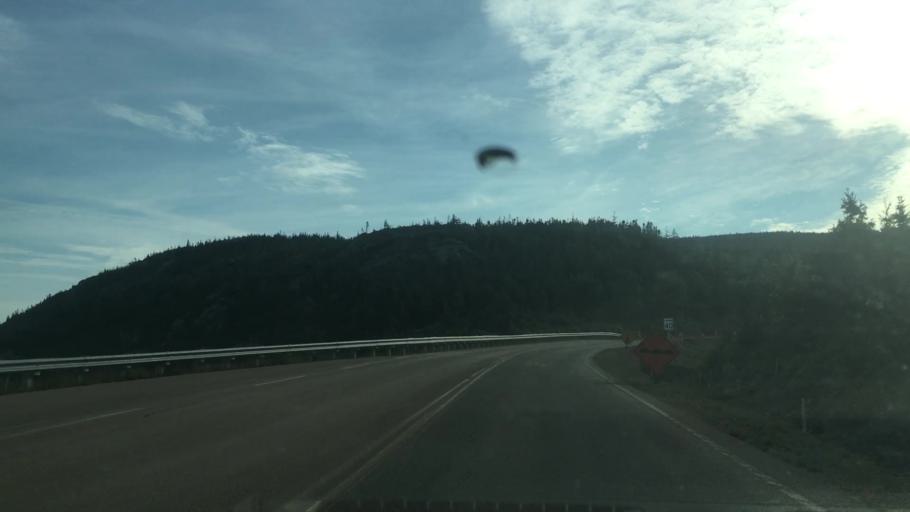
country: CA
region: Nova Scotia
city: Sydney Mines
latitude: 46.8175
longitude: -60.8338
